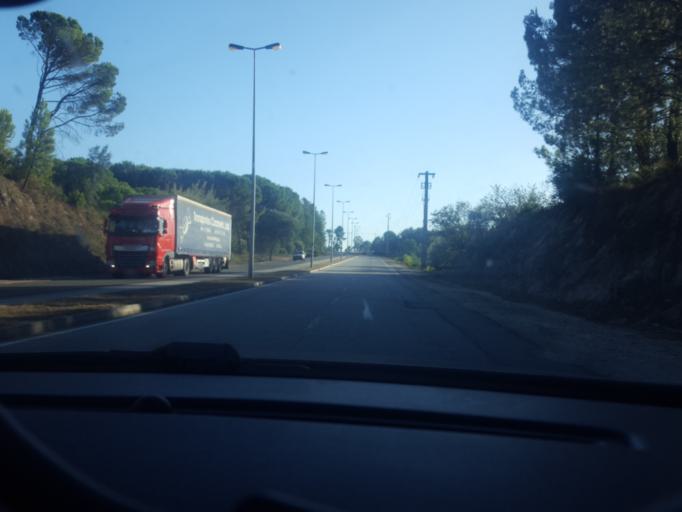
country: PT
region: Viseu
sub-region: Nelas
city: Nelas
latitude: 40.5321
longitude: -7.8640
